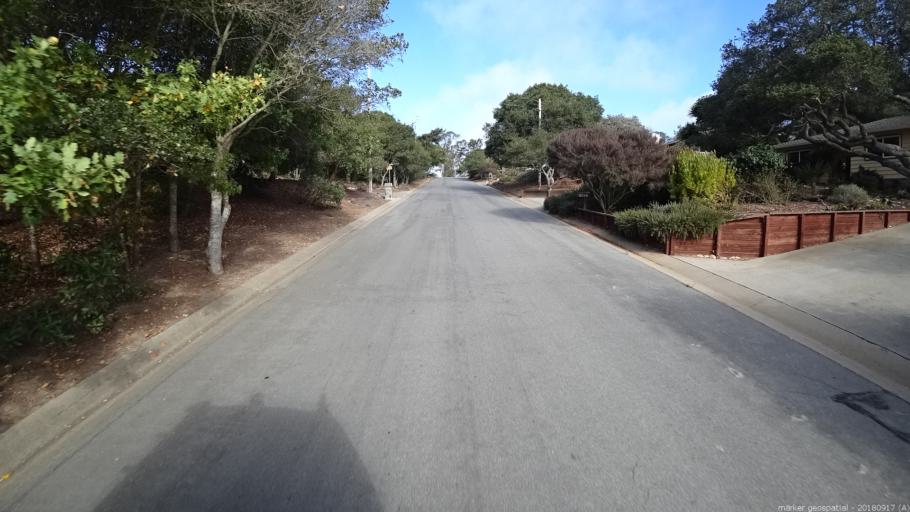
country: US
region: California
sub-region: Monterey County
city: Elkhorn
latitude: 36.8154
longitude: -121.7081
